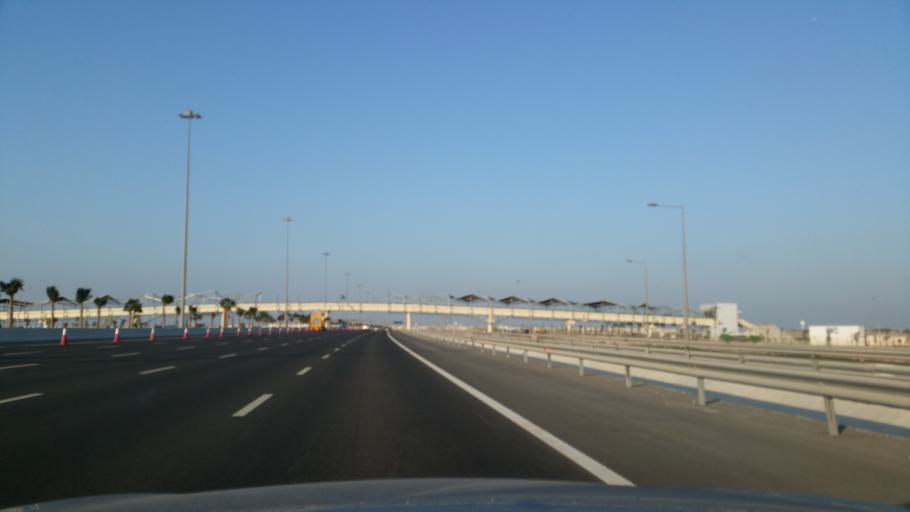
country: QA
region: Al Khawr
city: Al Khawr
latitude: 25.6455
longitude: 51.4948
